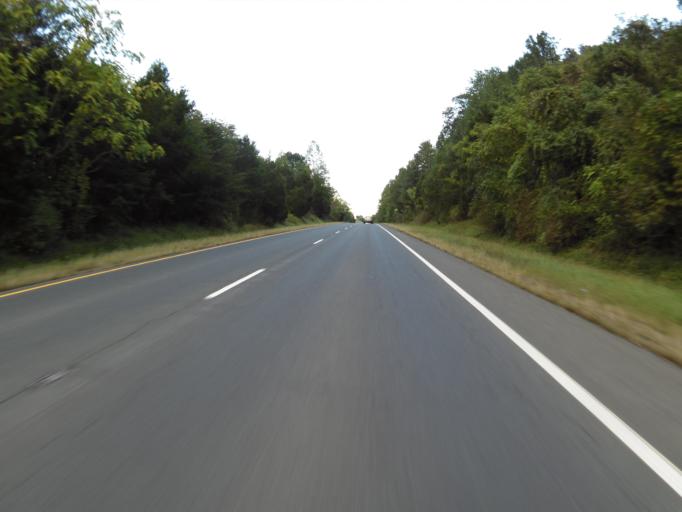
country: US
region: Virginia
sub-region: Fauquier County
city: Warrenton
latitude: 38.6993
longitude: -77.8834
